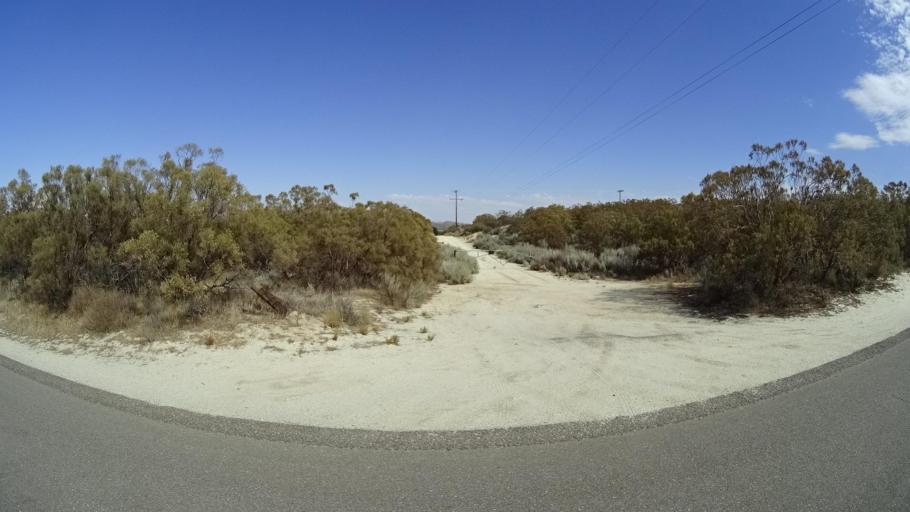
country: US
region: California
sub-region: San Diego County
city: Campo
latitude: 32.6881
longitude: -116.2937
